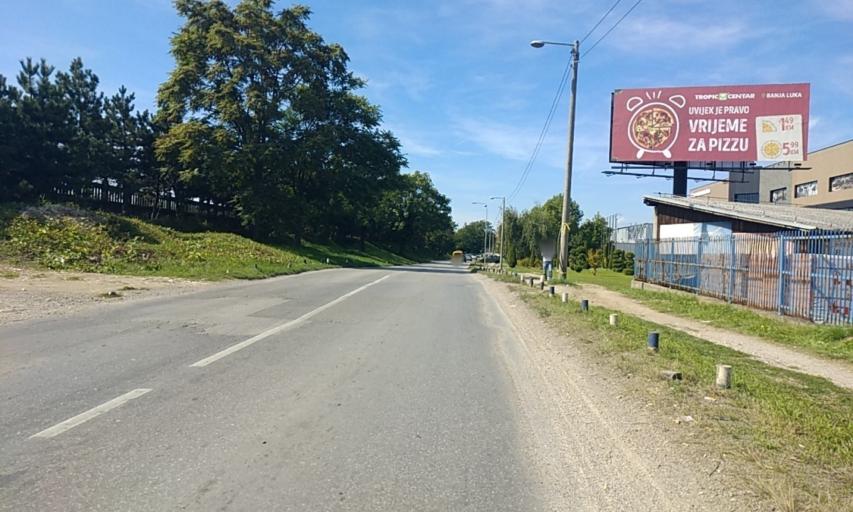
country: BA
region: Republika Srpska
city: Banja Luka
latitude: 44.7879
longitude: 17.2048
